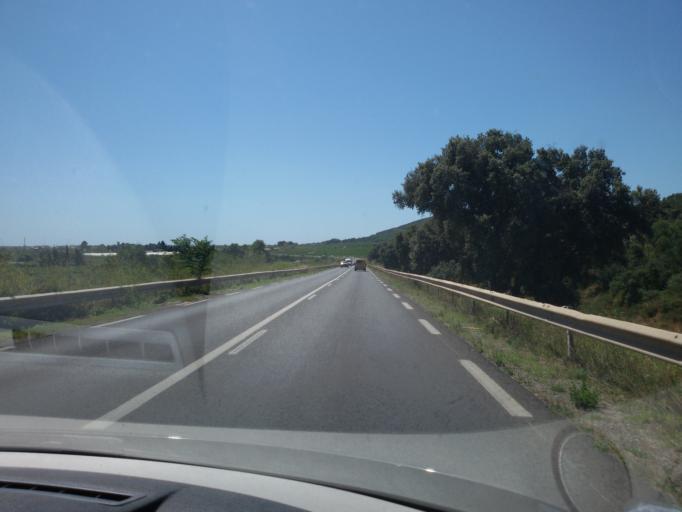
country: FR
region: Languedoc-Roussillon
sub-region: Departement de l'Herault
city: Vic-la-Gardiole
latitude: 43.4937
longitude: 3.7758
